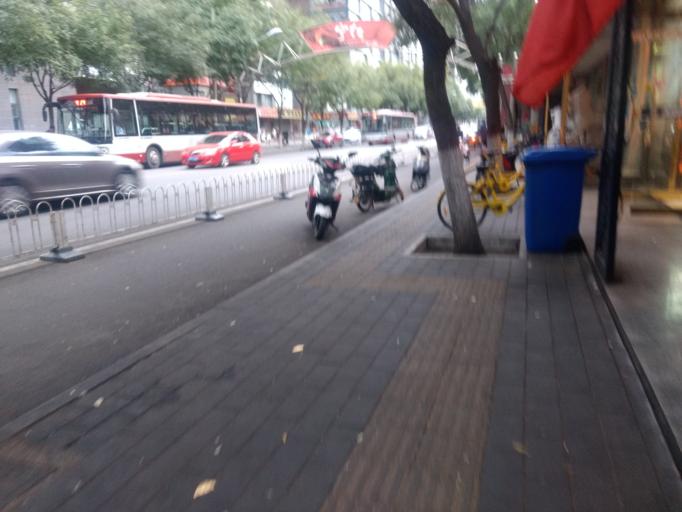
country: CN
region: Beijing
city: Baizhifang
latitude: 39.8849
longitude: 116.3206
